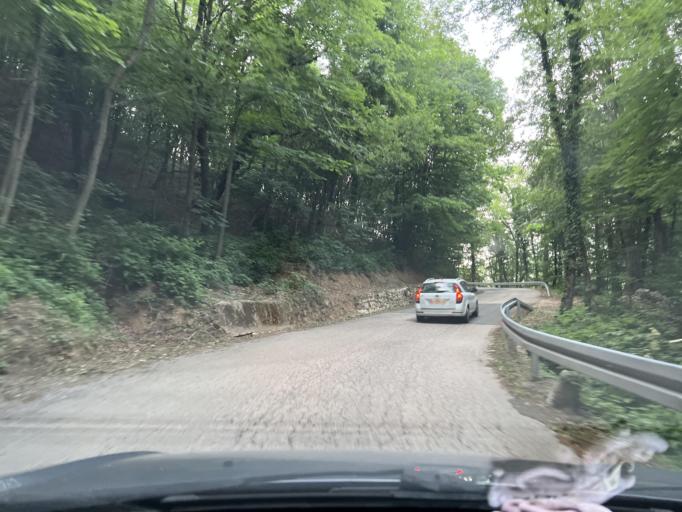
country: HR
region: Primorsko-Goranska
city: Marcelji
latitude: 45.3938
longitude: 14.4202
